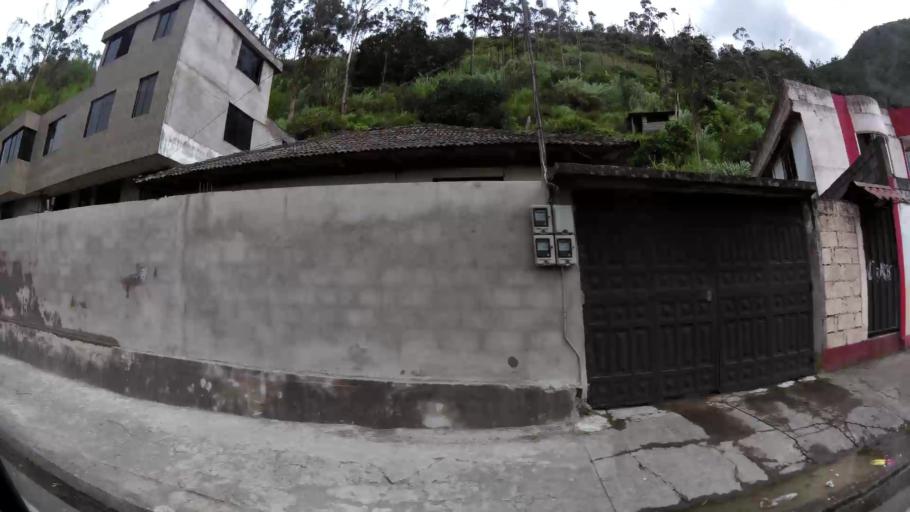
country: EC
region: Tungurahua
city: Banos
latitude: -1.3987
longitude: -78.4345
